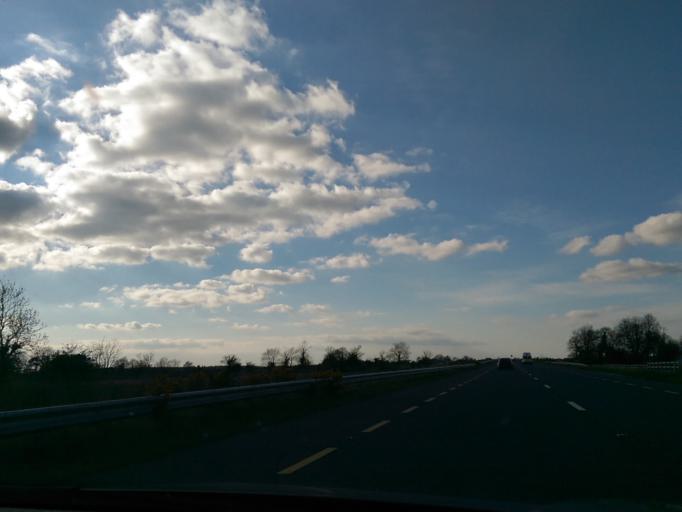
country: IE
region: Connaught
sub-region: County Galway
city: Loughrea
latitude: 53.2256
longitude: -8.5884
